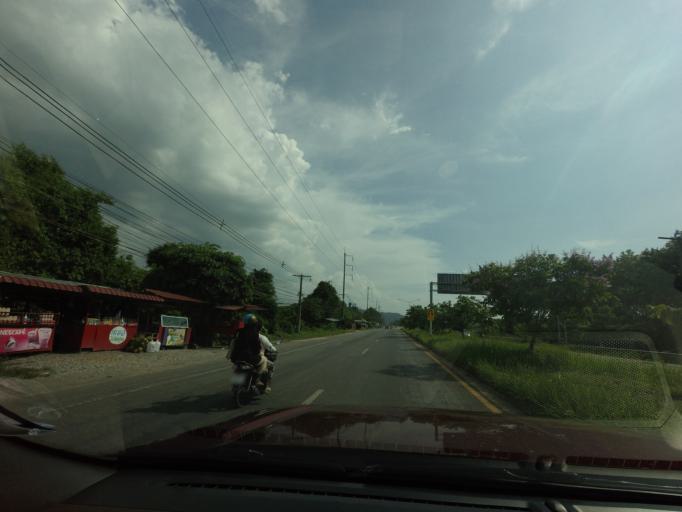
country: TH
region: Yala
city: Yala
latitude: 6.5509
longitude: 101.2579
